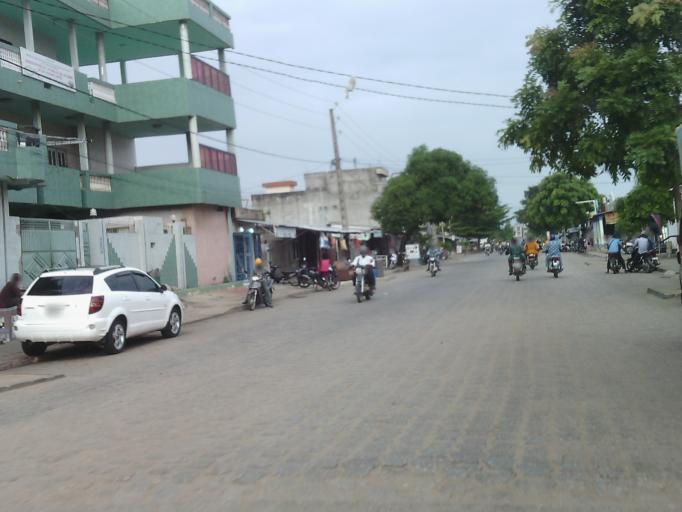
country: BJ
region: Littoral
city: Cotonou
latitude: 6.3881
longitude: 2.3792
